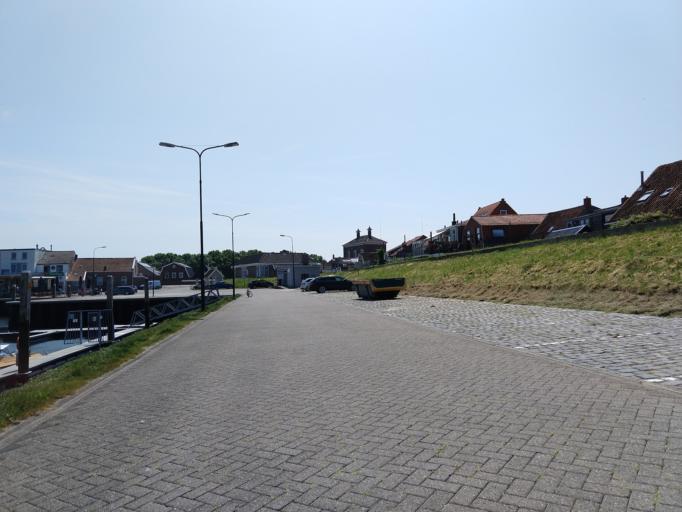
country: NL
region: Zeeland
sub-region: Gemeente Reimerswaal
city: Yerseke
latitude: 51.5887
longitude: 4.0124
